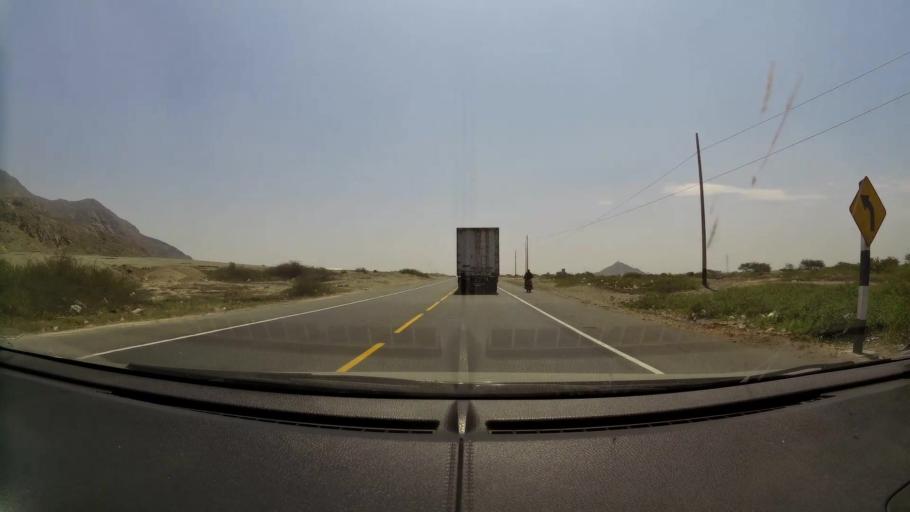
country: PE
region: La Libertad
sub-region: Provincia de Pacasmayo
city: Guadalupe
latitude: -7.2758
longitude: -79.4764
